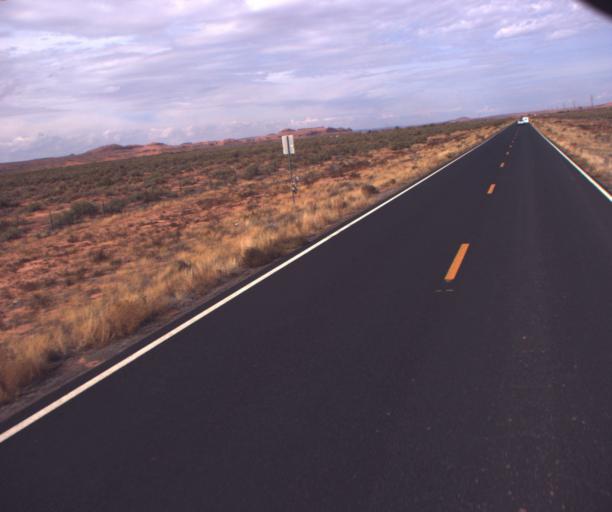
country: US
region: Arizona
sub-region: Apache County
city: Many Farms
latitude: 36.6632
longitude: -109.5965
